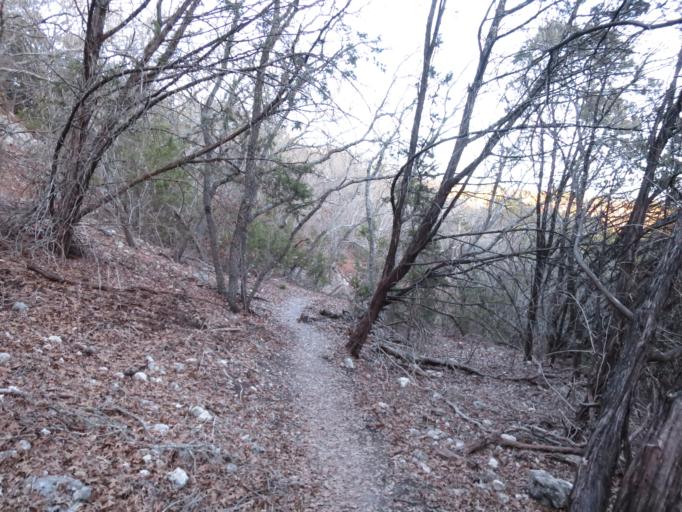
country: US
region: Texas
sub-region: Travis County
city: Lago Vista
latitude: 30.5047
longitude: -97.9870
